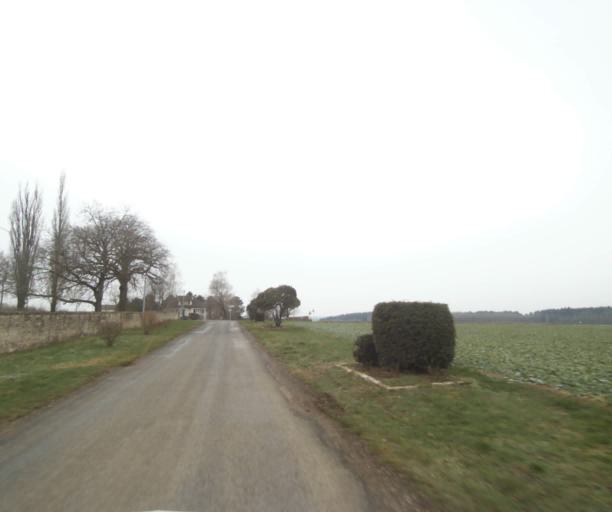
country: FR
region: Champagne-Ardenne
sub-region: Departement de la Haute-Marne
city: Chevillon
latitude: 48.4935
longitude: 5.0643
